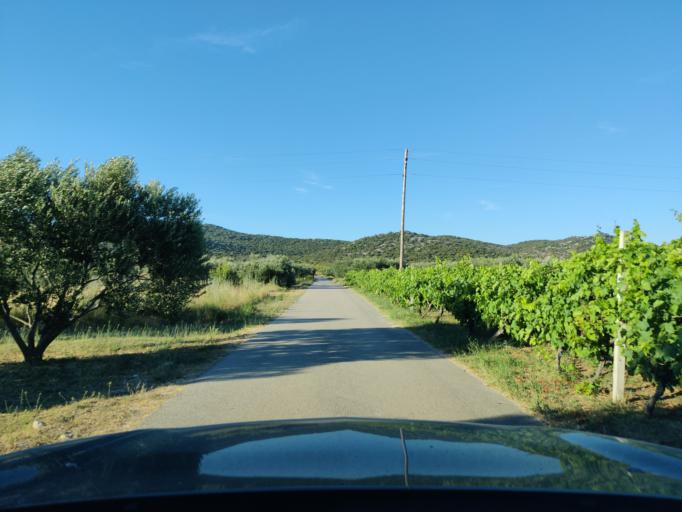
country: HR
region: Sibensko-Kniniska
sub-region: Grad Sibenik
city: Pirovac
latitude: 43.8627
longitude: 15.6964
